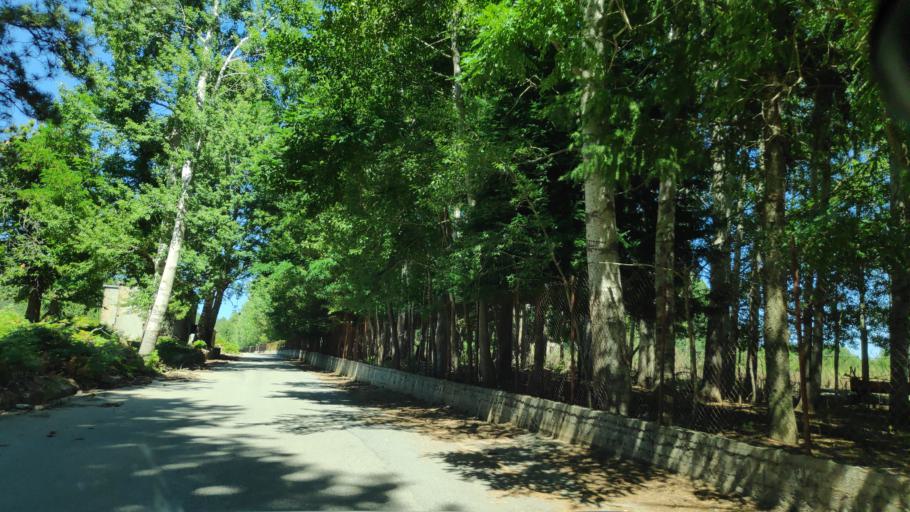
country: IT
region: Calabria
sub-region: Provincia di Reggio Calabria
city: Bova
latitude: 38.0289
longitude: 15.9445
